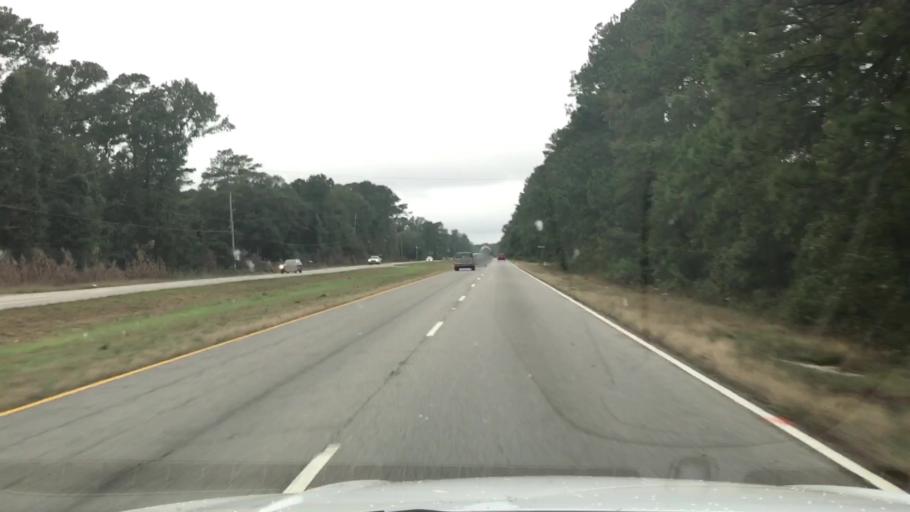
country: US
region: South Carolina
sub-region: Charleston County
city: Shell Point
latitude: 32.7807
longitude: -80.1686
